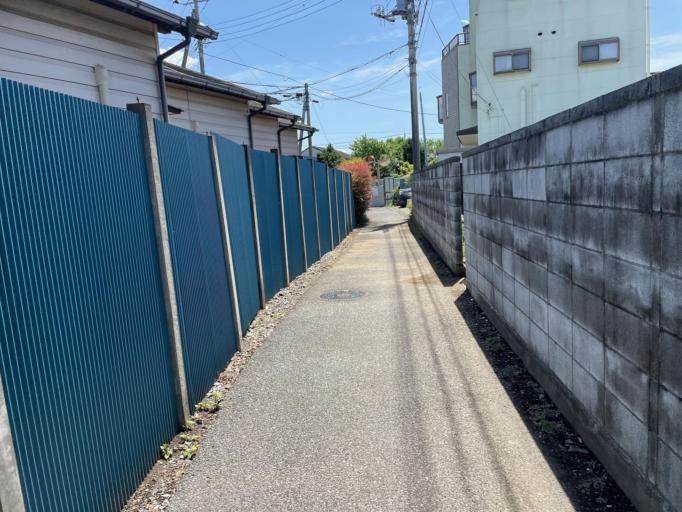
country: JP
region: Tochigi
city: Sano
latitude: 36.3237
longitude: 139.5863
